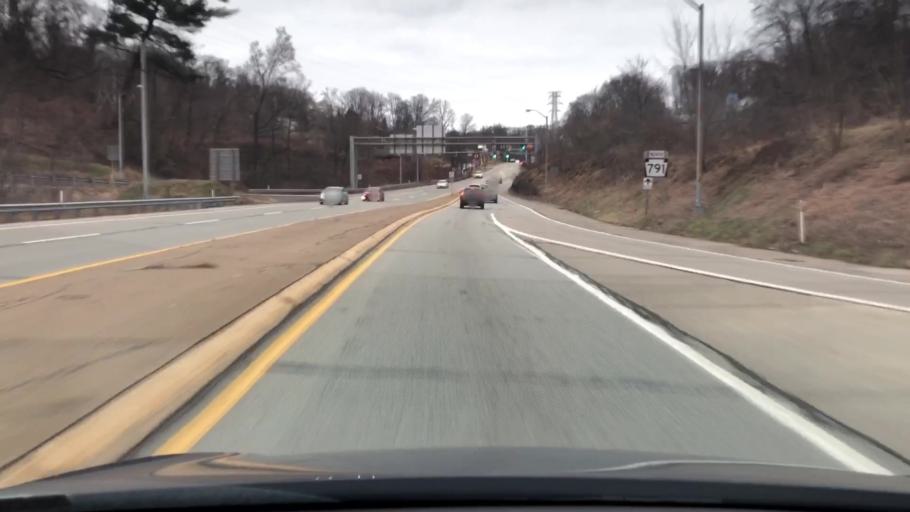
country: US
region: Pennsylvania
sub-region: Allegheny County
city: Churchill
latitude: 40.4433
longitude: -79.8284
